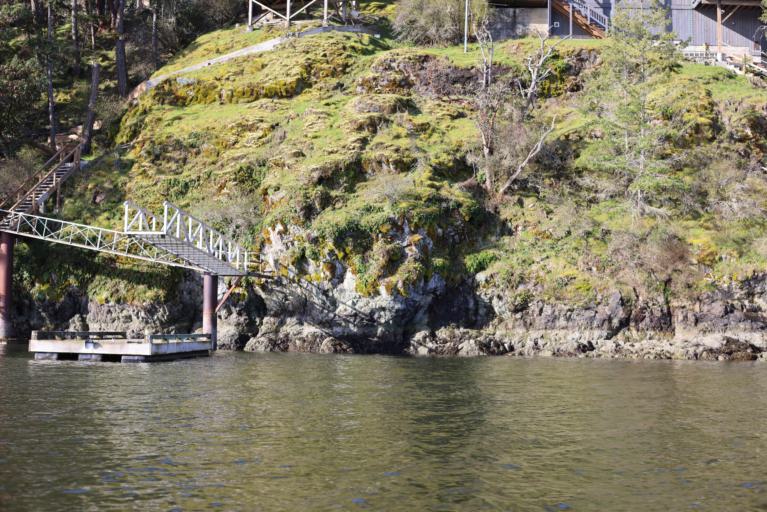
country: CA
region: British Columbia
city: North Saanich
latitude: 48.5739
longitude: -123.4744
